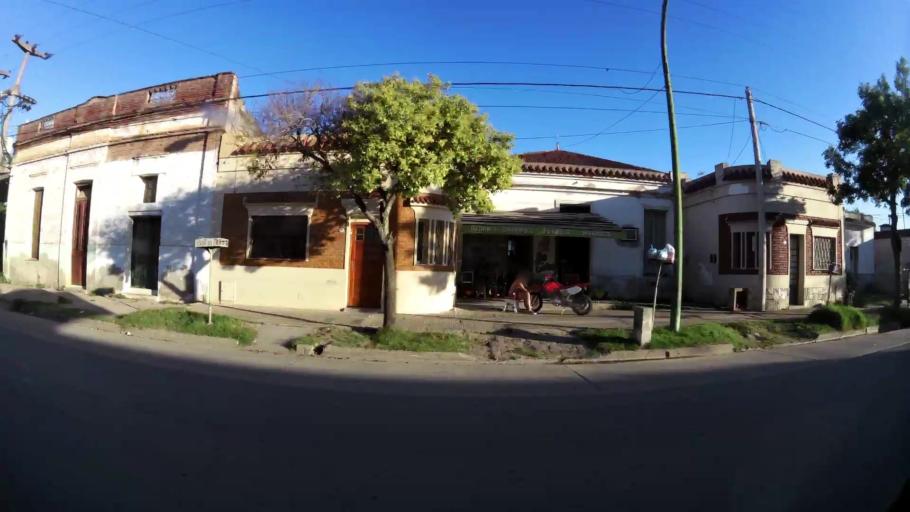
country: AR
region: Cordoba
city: Las Varillas
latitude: -31.8721
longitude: -62.7123
